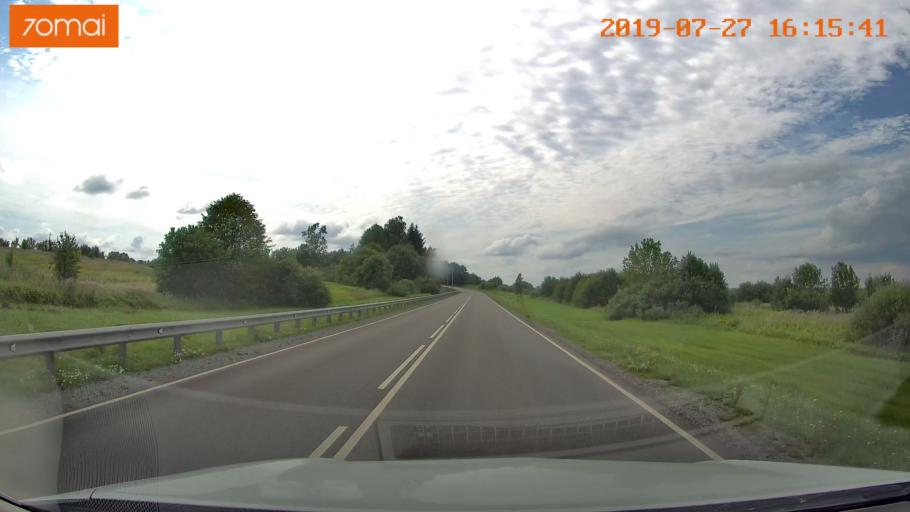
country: RU
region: Kaliningrad
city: Chernyakhovsk
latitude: 54.6250
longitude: 21.5895
